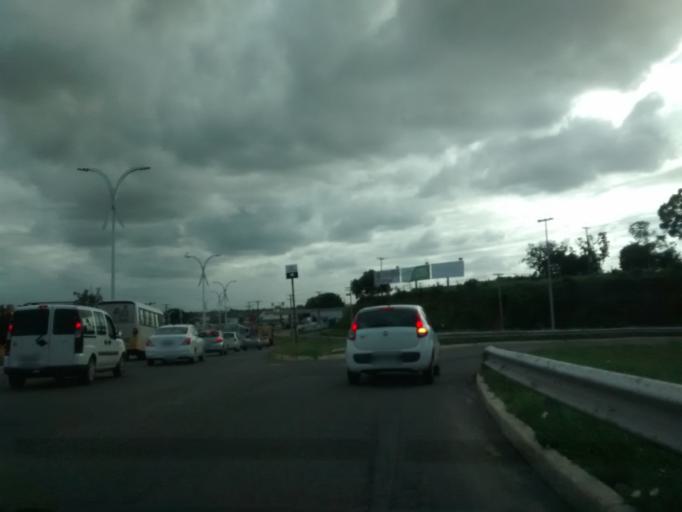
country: BR
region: Bahia
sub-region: Lauro De Freitas
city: Lauro de Freitas
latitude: -12.9204
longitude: -38.3533
